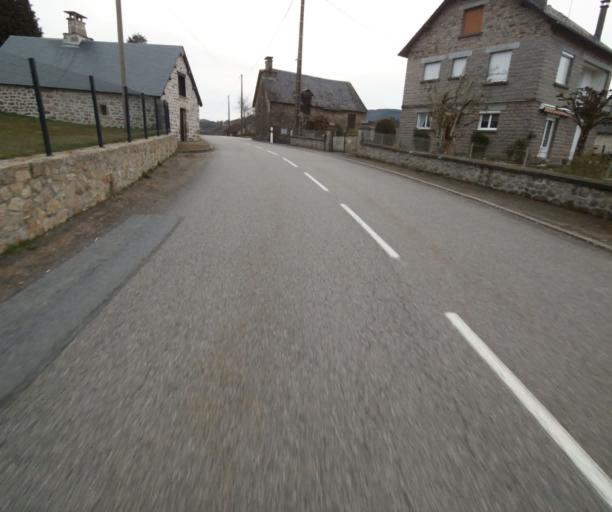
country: FR
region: Limousin
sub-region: Departement de la Correze
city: Correze
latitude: 45.4301
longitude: 1.8537
